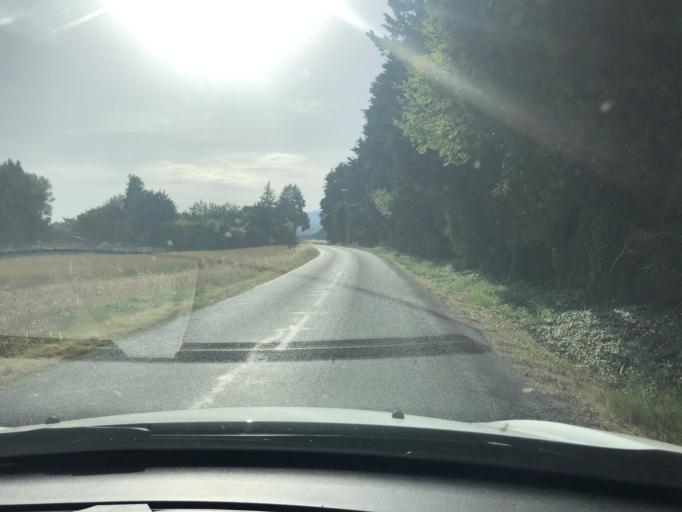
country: FR
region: Provence-Alpes-Cote d'Azur
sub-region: Departement du Vaucluse
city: Velleron
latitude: 43.9652
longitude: 5.0126
